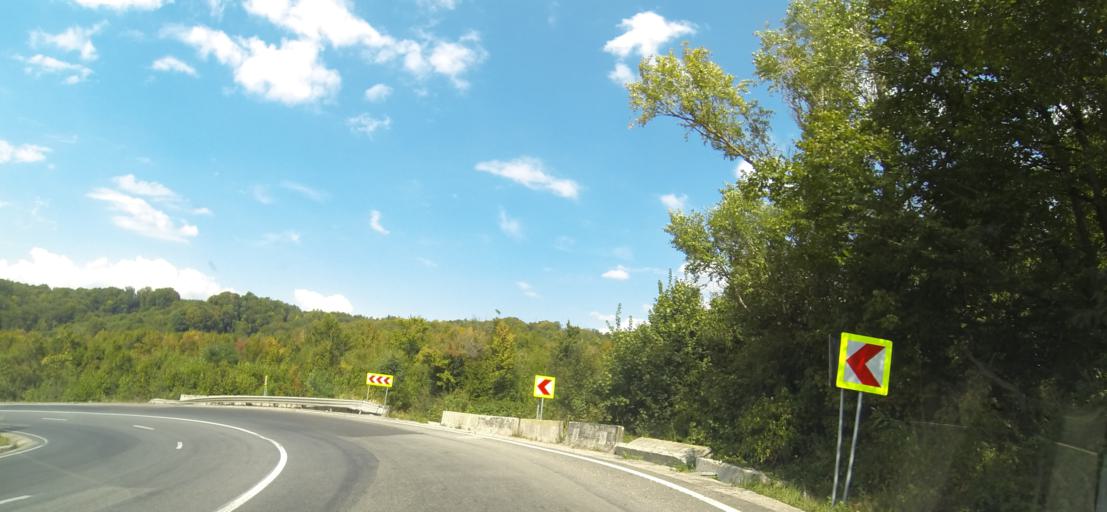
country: RO
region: Brasov
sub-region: Comuna Sinca Veche
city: Persani
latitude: 45.7550
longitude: 25.2757
